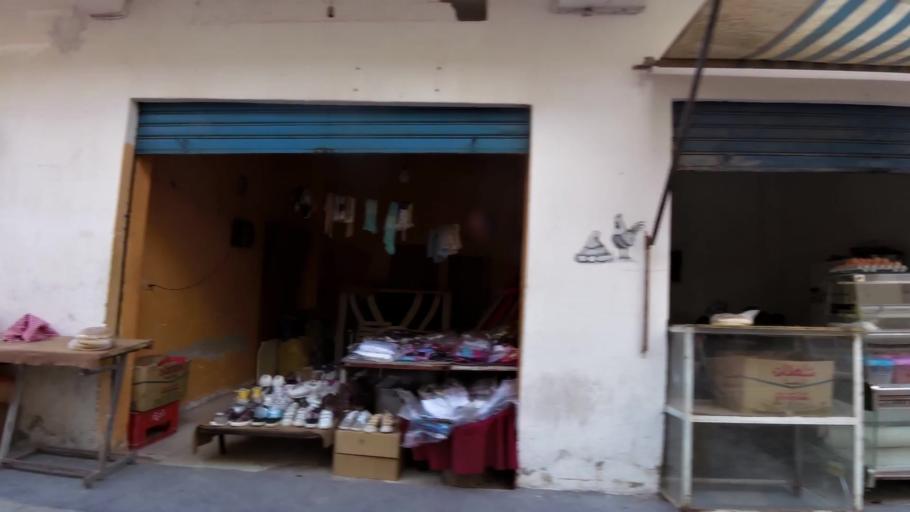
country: MA
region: Tanger-Tetouan
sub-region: Tetouan
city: Martil
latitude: 35.6117
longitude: -5.2730
